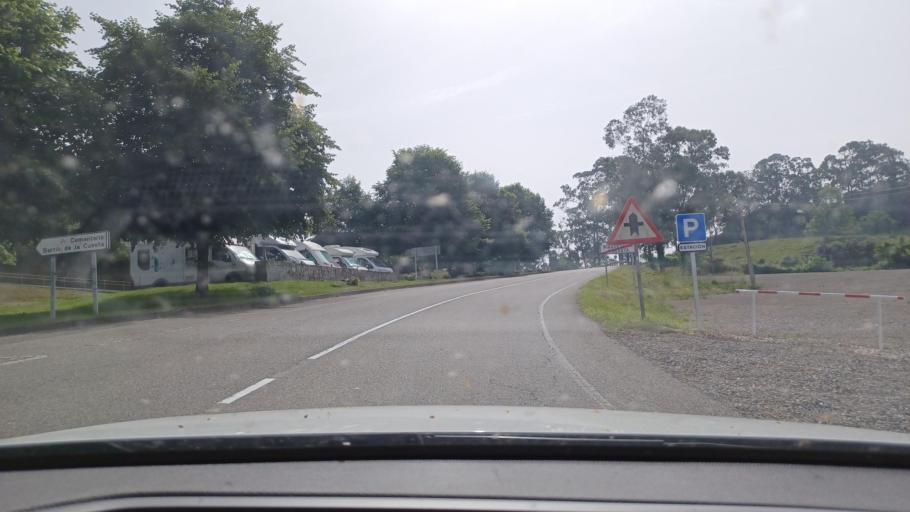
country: ES
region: Asturias
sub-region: Province of Asturias
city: Ribadesella
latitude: 43.4602
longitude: -5.0547
